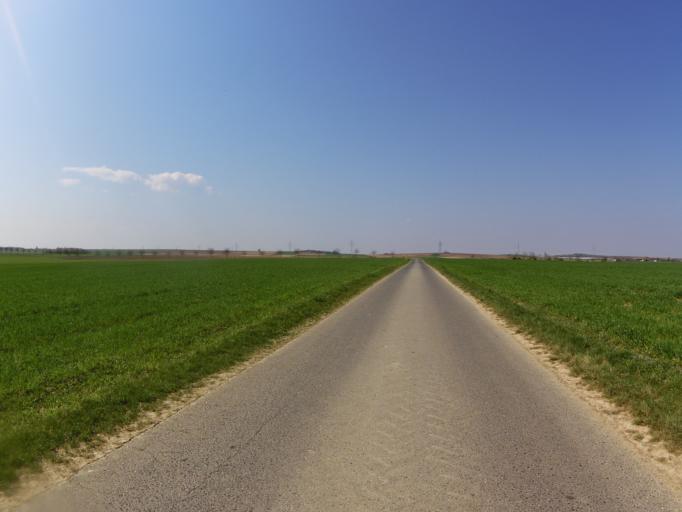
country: DE
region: Bavaria
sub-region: Regierungsbezirk Unterfranken
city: Mainstockheim
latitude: 49.8141
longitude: 10.1099
